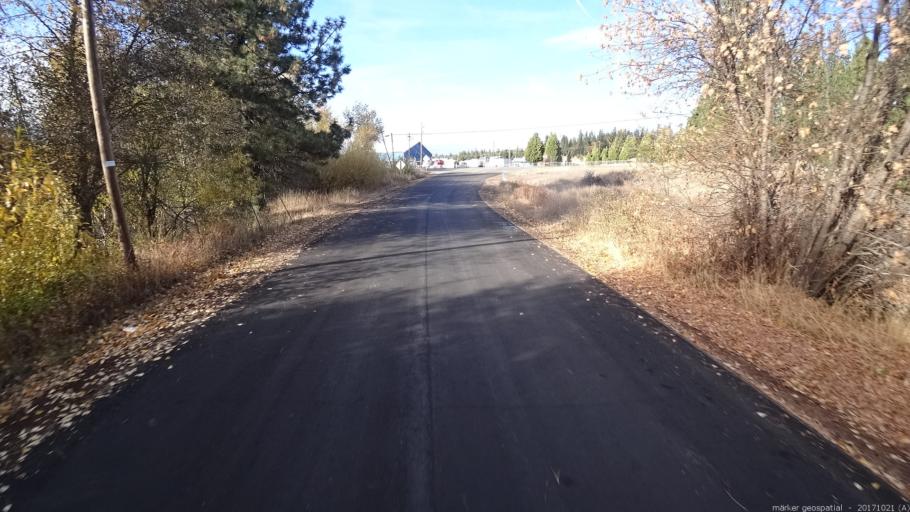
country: US
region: California
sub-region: Shasta County
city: Burney
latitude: 40.8722
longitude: -121.6976
